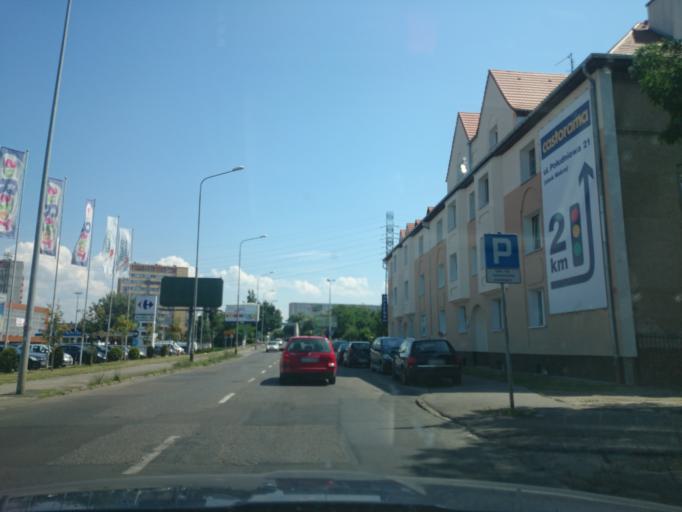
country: PL
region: West Pomeranian Voivodeship
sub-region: Szczecin
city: Szczecin
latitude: 53.4097
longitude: 14.5206
